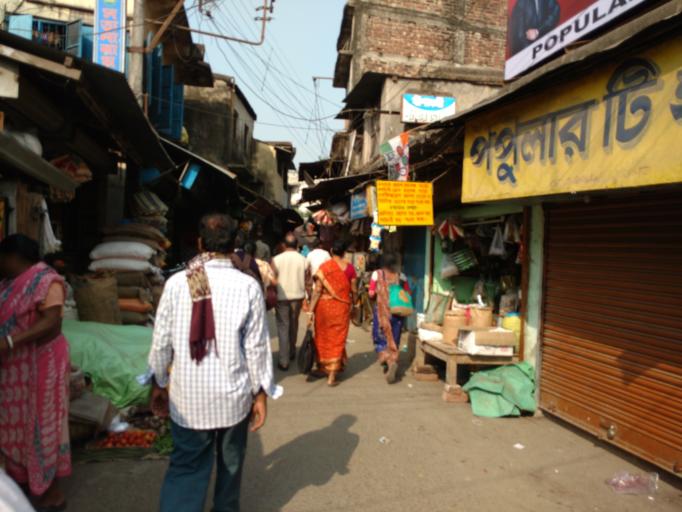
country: IN
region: West Bengal
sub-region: South 24 Paraganas
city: Champahati
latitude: 22.4423
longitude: 88.4319
